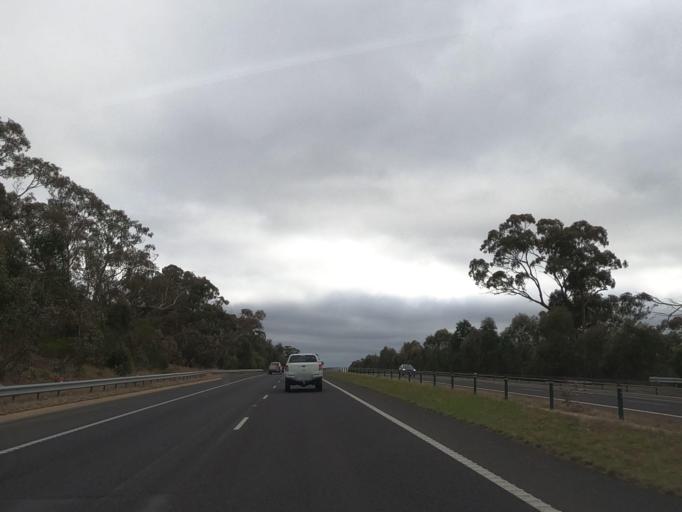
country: AU
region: Victoria
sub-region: Mount Alexander
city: Castlemaine
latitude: -37.0323
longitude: 144.2754
